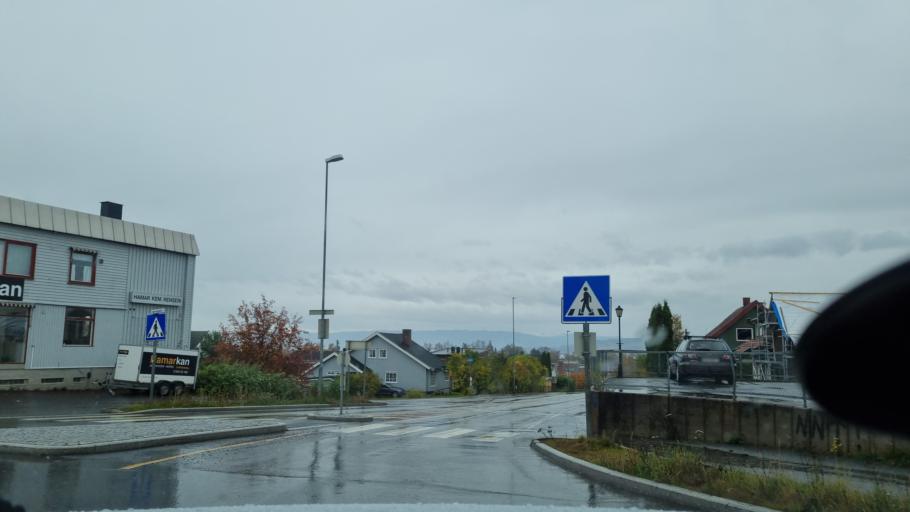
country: NO
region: Hedmark
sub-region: Hamar
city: Hamar
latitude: 60.8028
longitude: 11.0473
